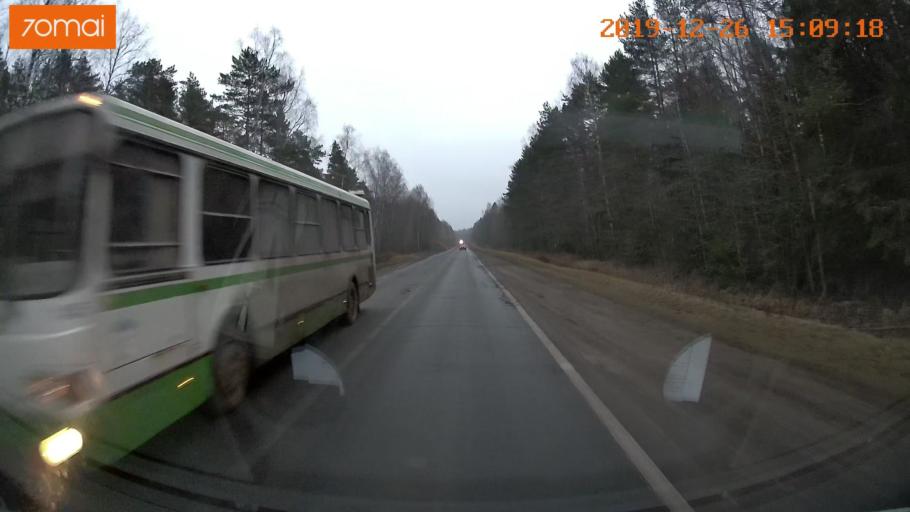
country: RU
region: Jaroslavl
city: Rybinsk
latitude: 58.1504
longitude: 38.8393
